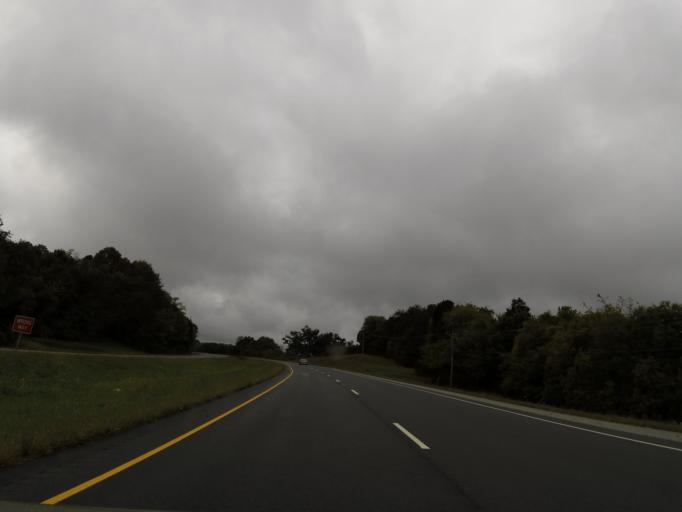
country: US
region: Tennessee
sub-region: Loudon County
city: Greenback
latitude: 35.7555
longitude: -84.1326
